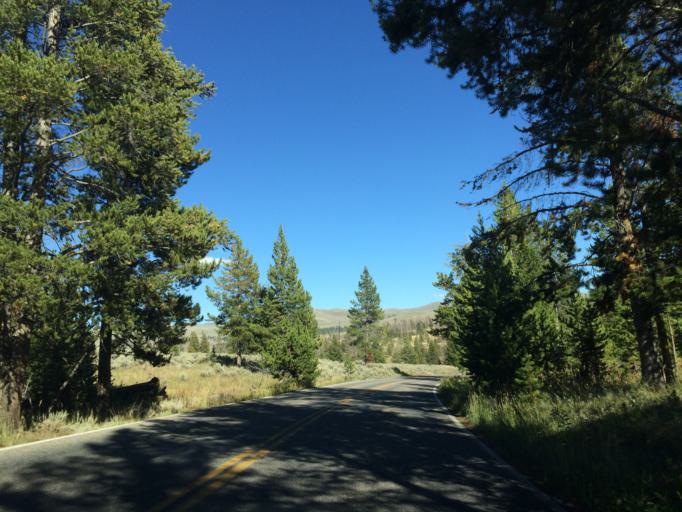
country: US
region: Montana
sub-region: Gallatin County
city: West Yellowstone
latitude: 44.8644
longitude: -110.3975
